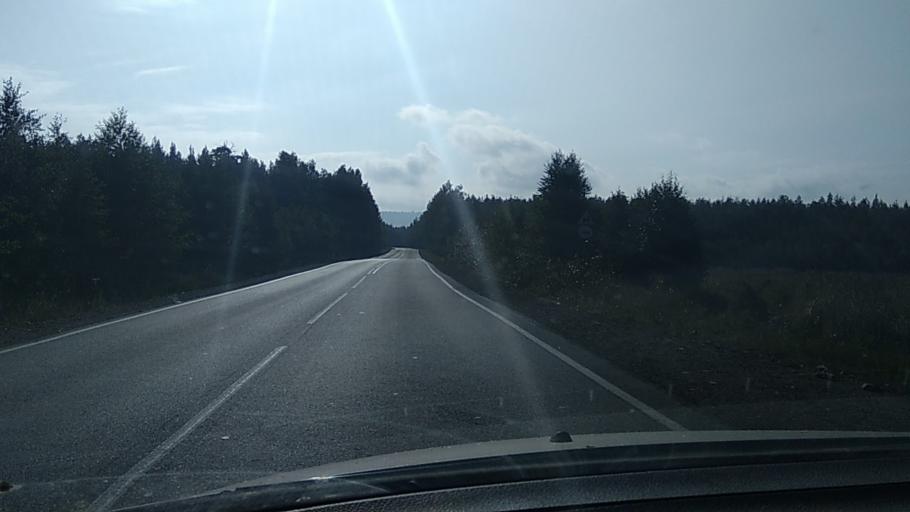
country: RU
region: Chelyabinsk
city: Karabash
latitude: 55.4325
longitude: 60.2507
